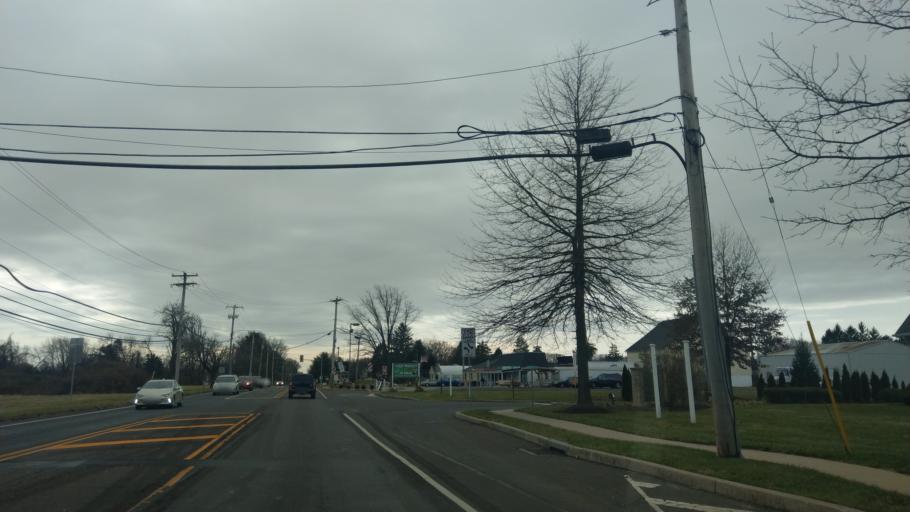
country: US
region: Pennsylvania
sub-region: Bucks County
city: Hulmeville
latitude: 40.1272
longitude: -74.9245
